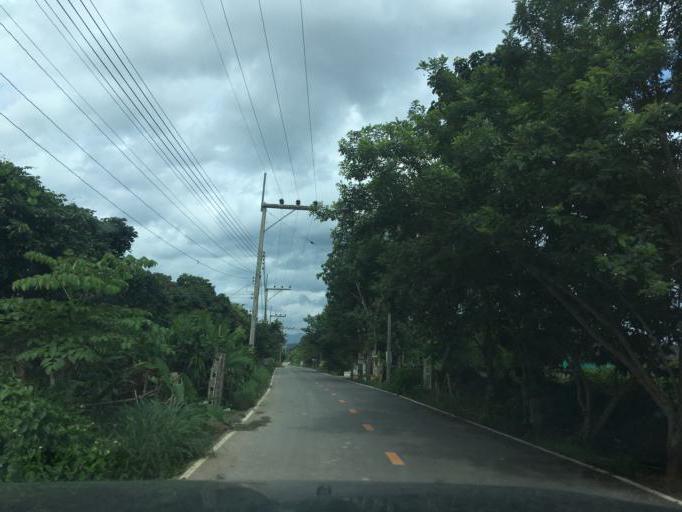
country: TH
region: Chiang Rai
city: Wiang Pa Pao
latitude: 19.2337
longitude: 99.4928
